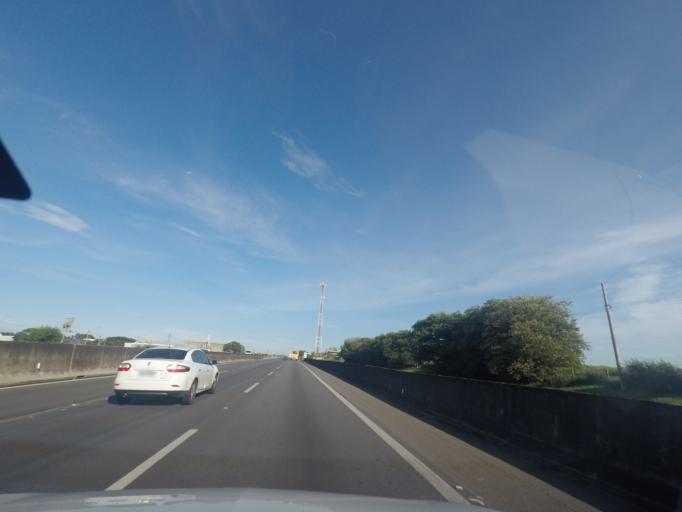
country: BR
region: Sao Paulo
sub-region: Nova Odessa
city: Nova Odessa
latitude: -22.7395
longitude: -47.2743
